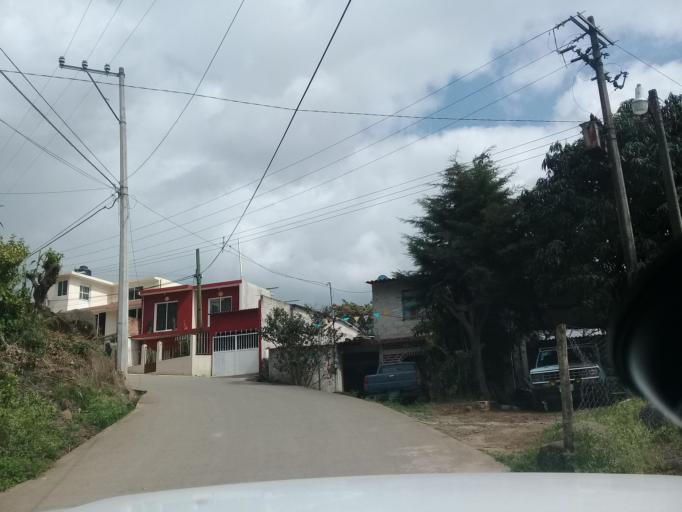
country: MX
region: Veracruz
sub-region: Xalapa
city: Fraccionamiento las Fuentes
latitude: 19.4753
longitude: -96.8774
